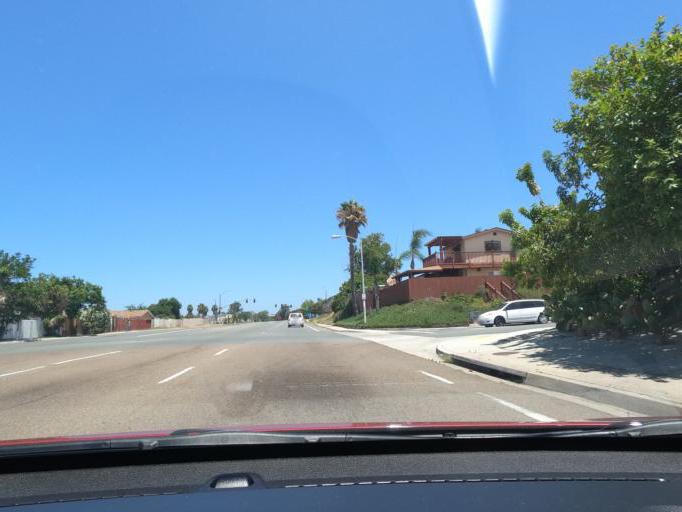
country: US
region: California
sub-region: San Diego County
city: Imperial Beach
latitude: 32.5719
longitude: -117.0536
